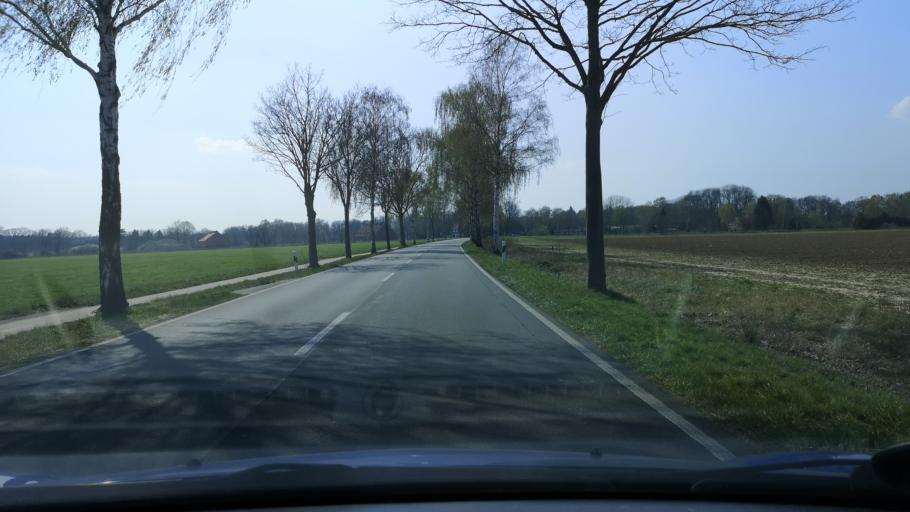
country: DE
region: Lower Saxony
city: Neustadt am Rubenberge
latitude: 52.5077
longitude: 9.5065
